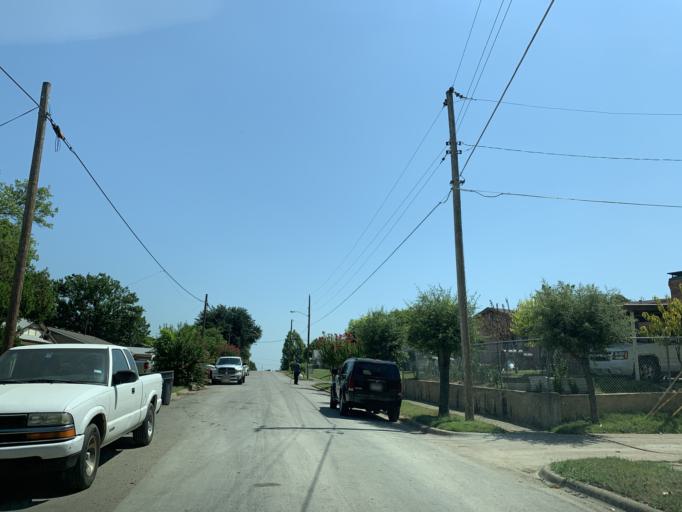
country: US
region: Texas
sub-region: Dallas County
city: Hutchins
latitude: 32.6765
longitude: -96.7539
